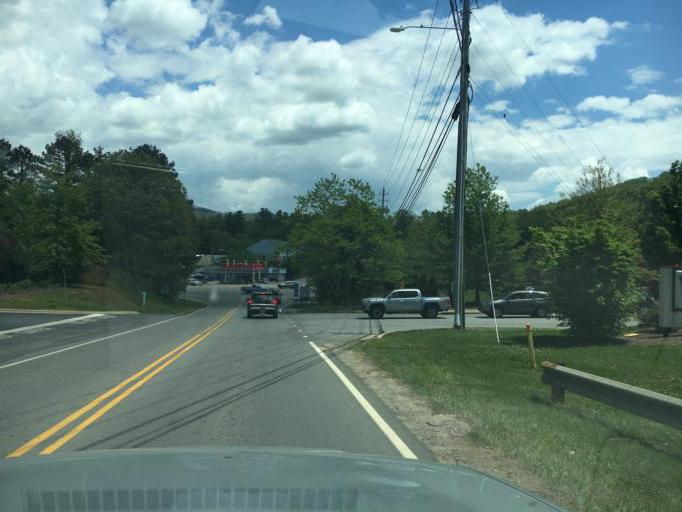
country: US
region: North Carolina
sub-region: Buncombe County
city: Weaverville
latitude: 35.7116
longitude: -82.5623
